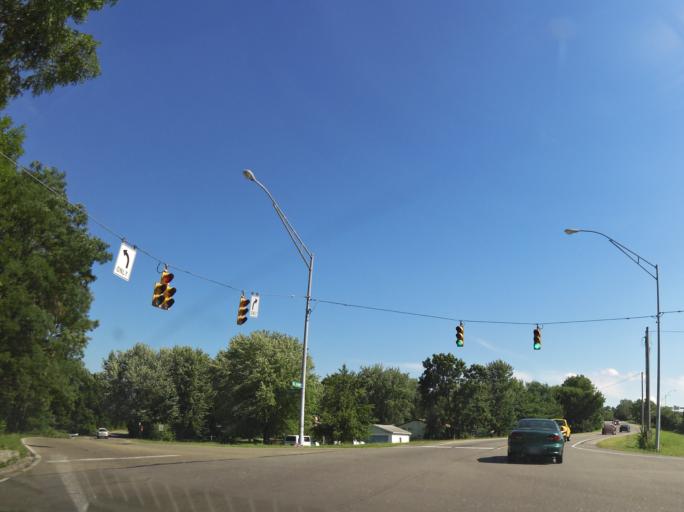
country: US
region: Ohio
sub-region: Greene County
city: Wright-Patterson AFB
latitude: 39.7883
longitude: -84.0439
